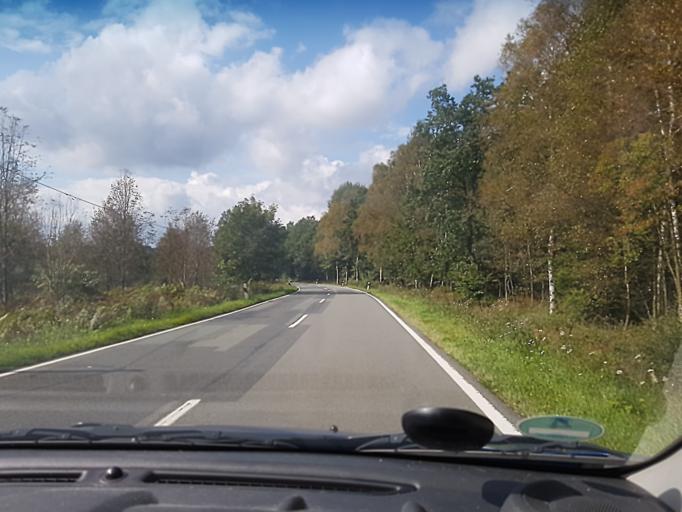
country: DE
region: Lower Saxony
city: Arholzen
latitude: 51.7692
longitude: 9.5581
